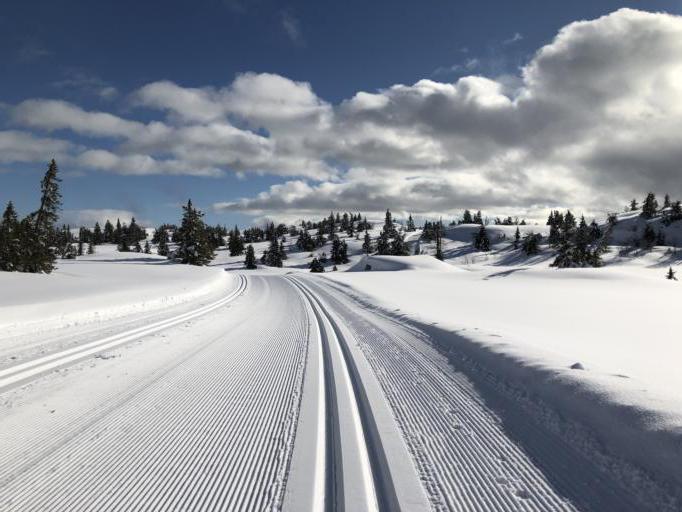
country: NO
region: Oppland
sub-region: Gausdal
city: Segalstad bru
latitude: 61.3304
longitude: 10.0329
